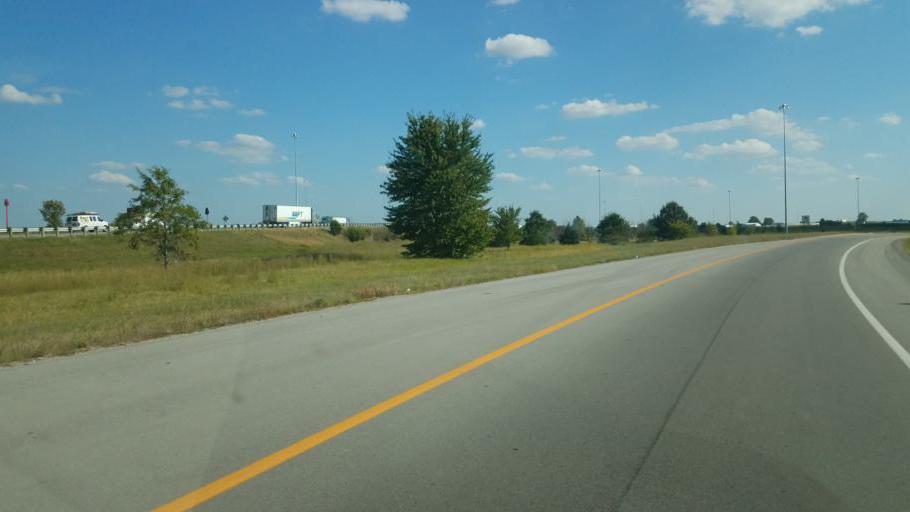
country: US
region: Ohio
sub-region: Wyandot County
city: Upper Sandusky
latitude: 40.8364
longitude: -83.2444
